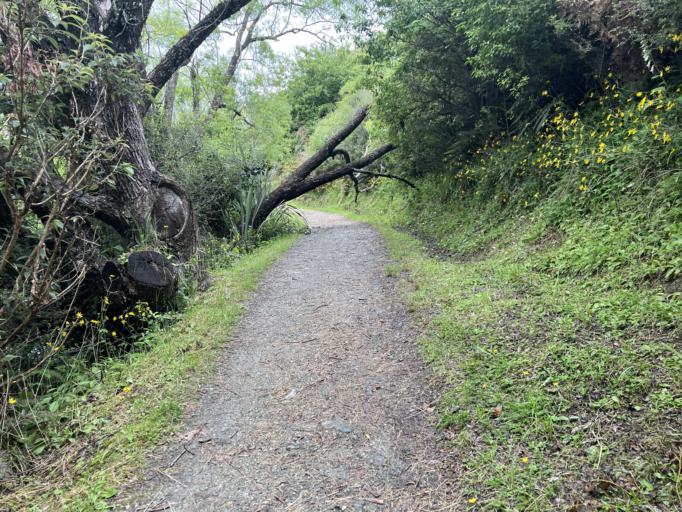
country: NZ
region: Otago
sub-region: Queenstown-Lakes District
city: Wanaka
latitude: -44.6472
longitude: 168.9624
